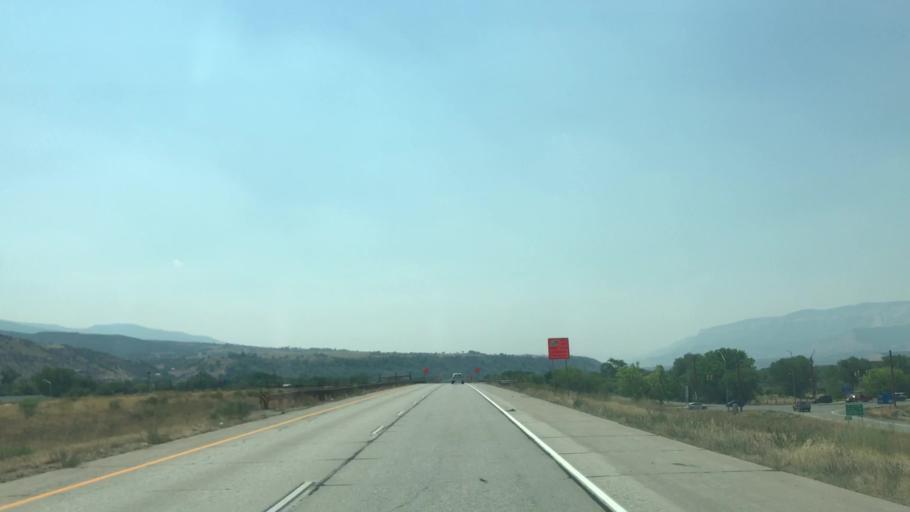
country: US
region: Colorado
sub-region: Garfield County
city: Rifle
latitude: 39.5248
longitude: -107.7754
